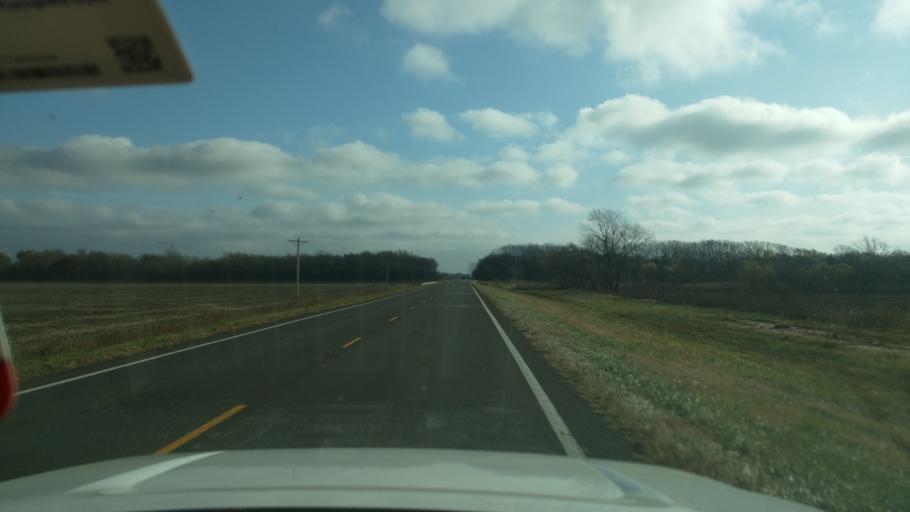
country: US
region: Kansas
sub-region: Montgomery County
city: Caney
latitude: 37.0679
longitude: -95.9962
